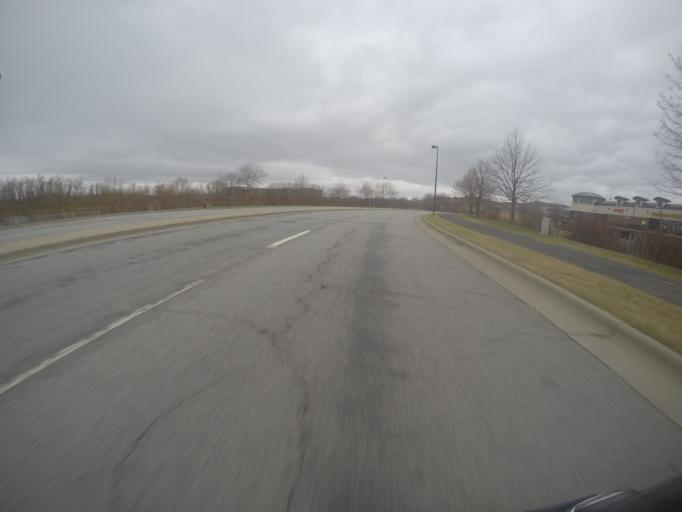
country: US
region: Minnesota
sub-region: Hennepin County
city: Eden Prairie
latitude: 44.8587
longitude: -93.4426
